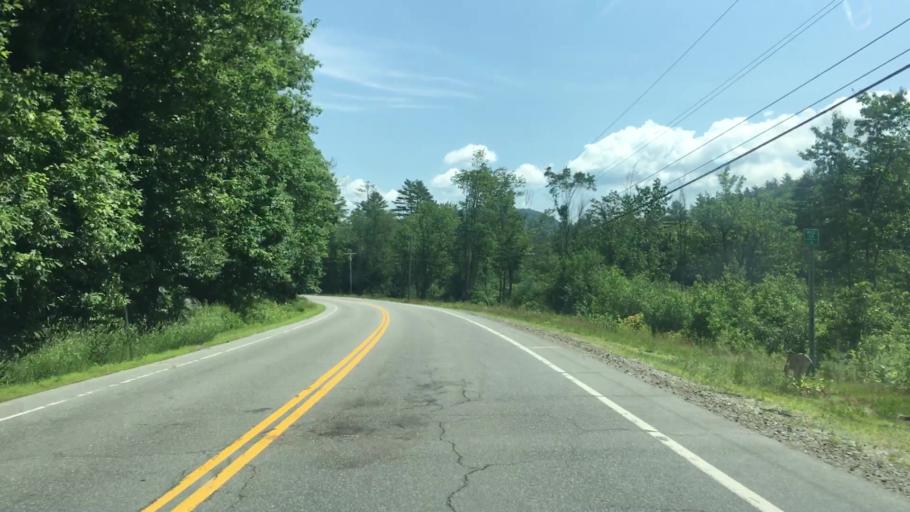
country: US
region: New Hampshire
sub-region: Sullivan County
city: Grantham
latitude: 43.4331
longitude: -72.1602
